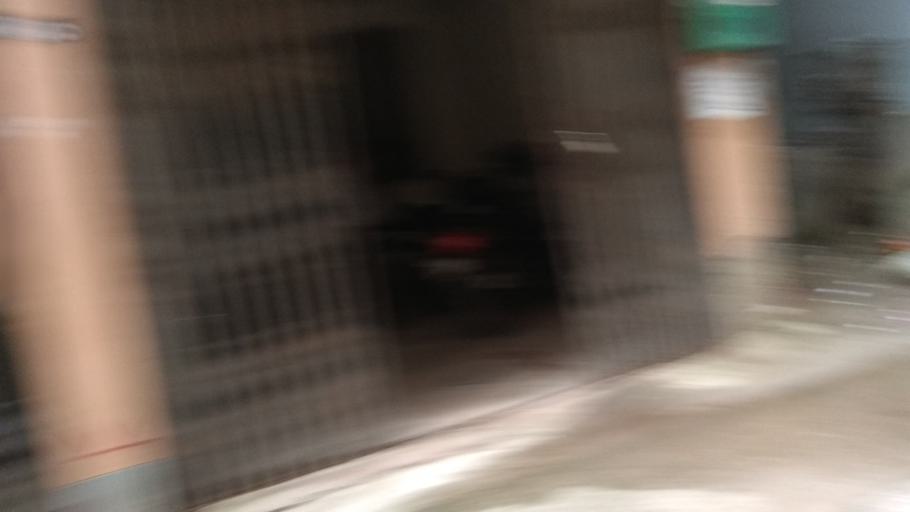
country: BD
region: Dhaka
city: Tungi
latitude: 23.8210
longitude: 90.3740
